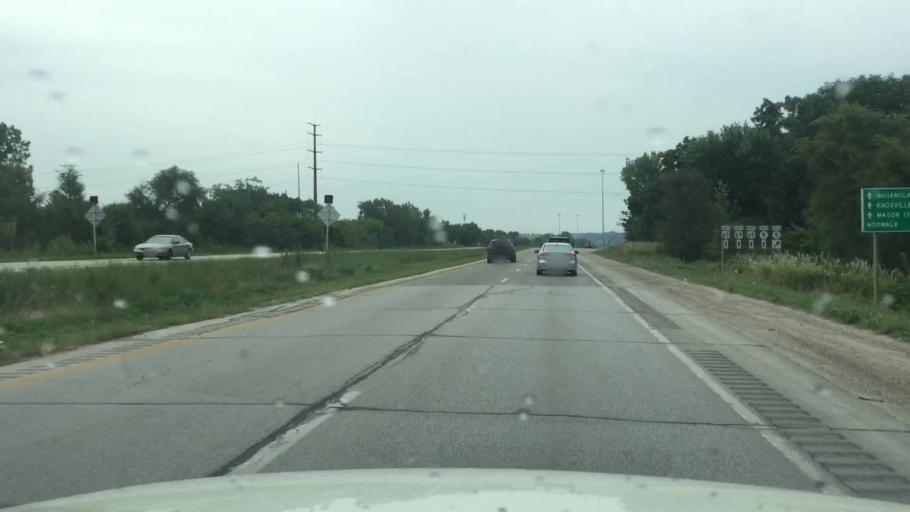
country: US
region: Iowa
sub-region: Warren County
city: Carlisle
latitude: 41.5116
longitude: -93.5778
